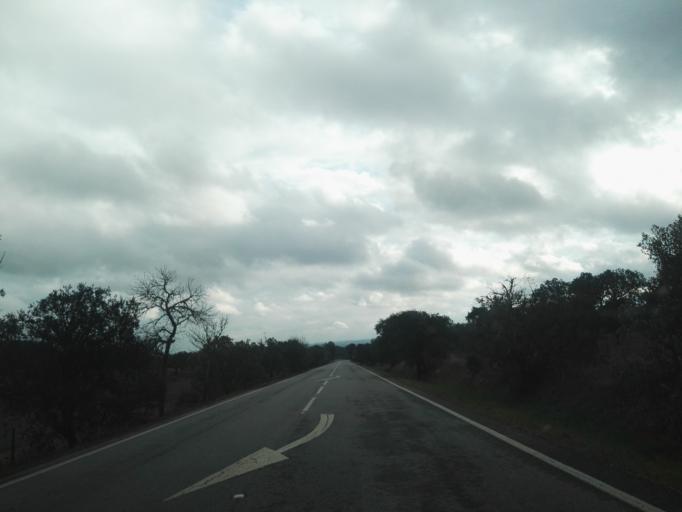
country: PT
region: Portalegre
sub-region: Arronches
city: Arronches
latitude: 39.0778
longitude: -7.2794
